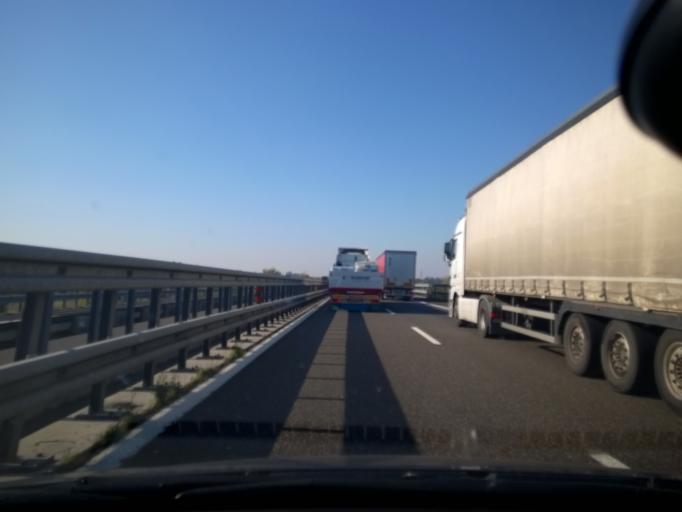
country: IT
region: Emilia-Romagna
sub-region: Provincia di Piacenza
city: San Nicolo
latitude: 45.0621
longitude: 9.6380
